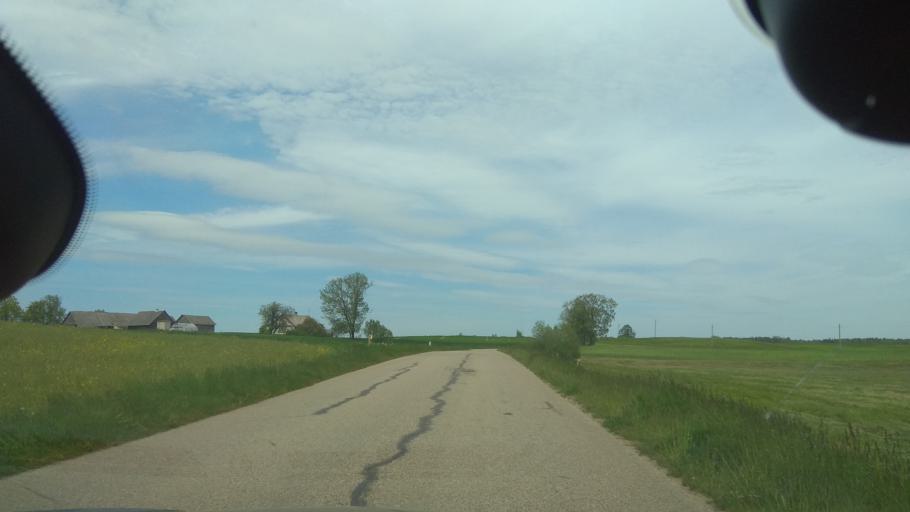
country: LT
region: Vilnius County
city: Ukmerge
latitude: 55.1543
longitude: 24.5444
